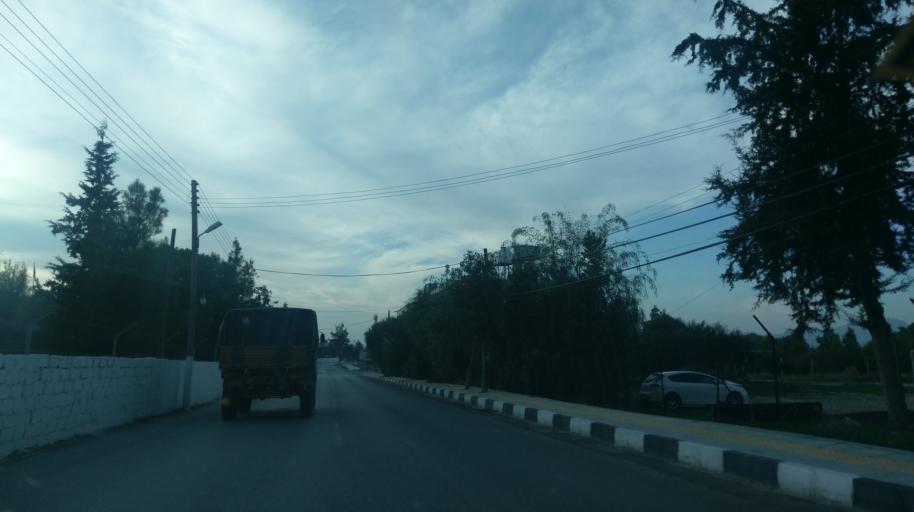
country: CY
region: Larnaka
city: Athienou
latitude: 35.1594
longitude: 33.6016
